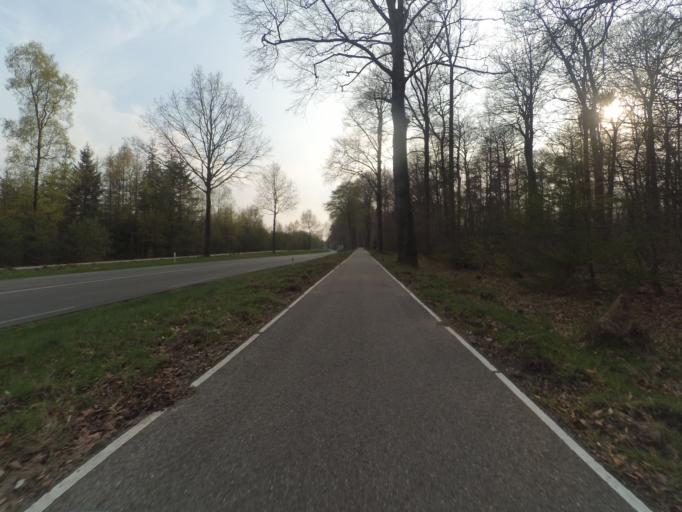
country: NL
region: Gelderland
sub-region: Gemeente Apeldoorn
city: Beekbergen
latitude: 52.1605
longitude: 5.8957
